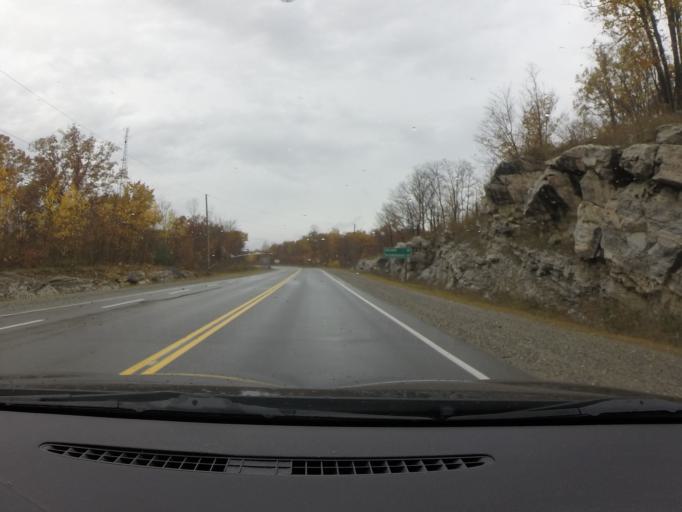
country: CA
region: Ontario
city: Perth
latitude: 44.7949
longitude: -76.6964
